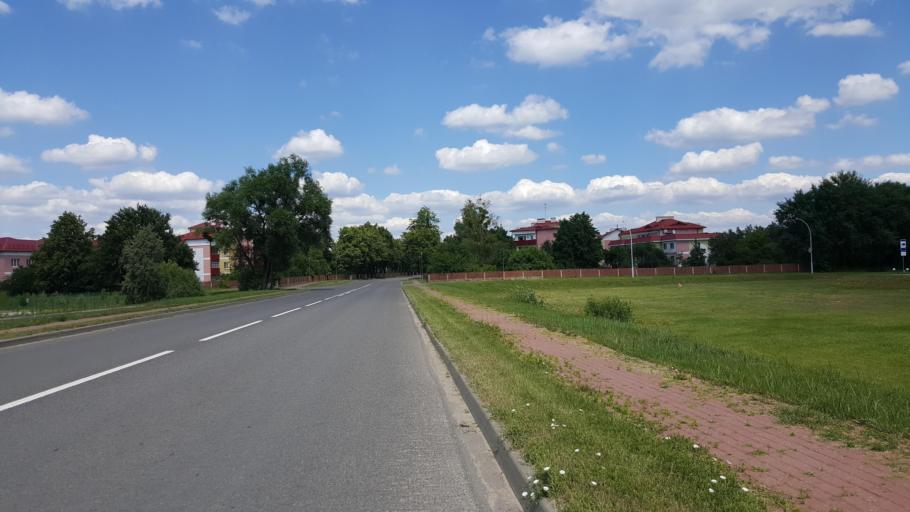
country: BY
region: Brest
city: Kamyanyuki
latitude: 52.5542
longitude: 23.7943
